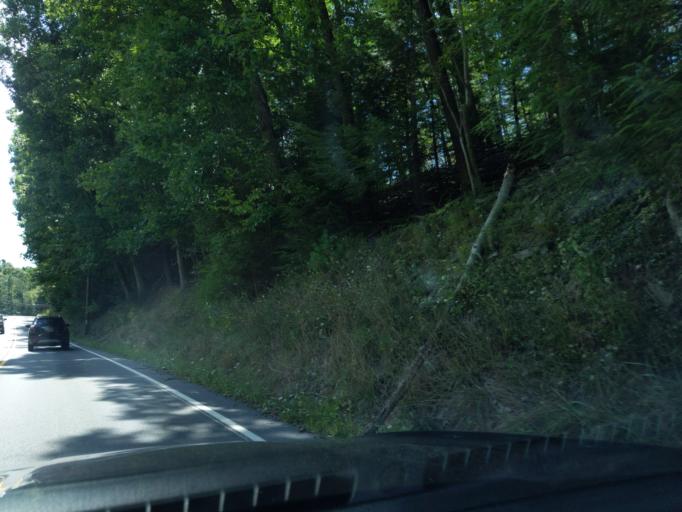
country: US
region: Pennsylvania
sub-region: Blair County
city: Greenwood
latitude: 40.5195
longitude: -78.3064
